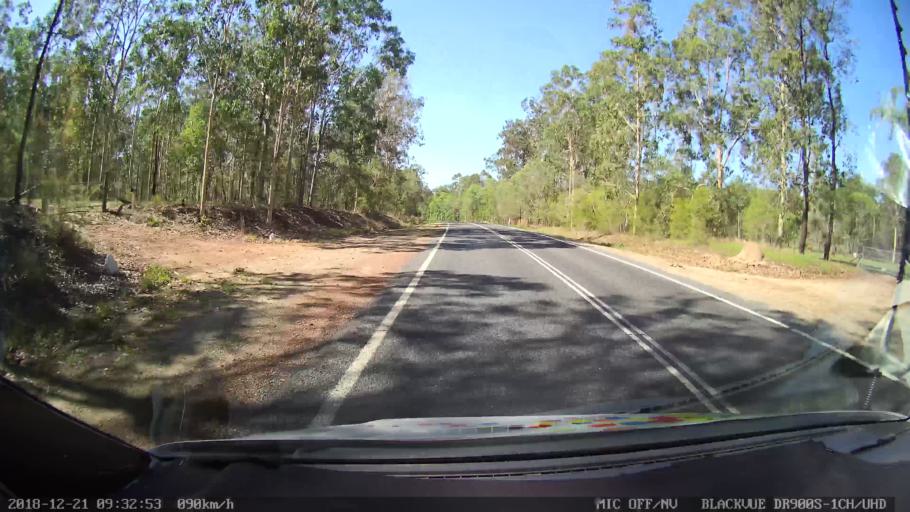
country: AU
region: New South Wales
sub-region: Clarence Valley
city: Grafton
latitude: -29.4766
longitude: 152.9765
